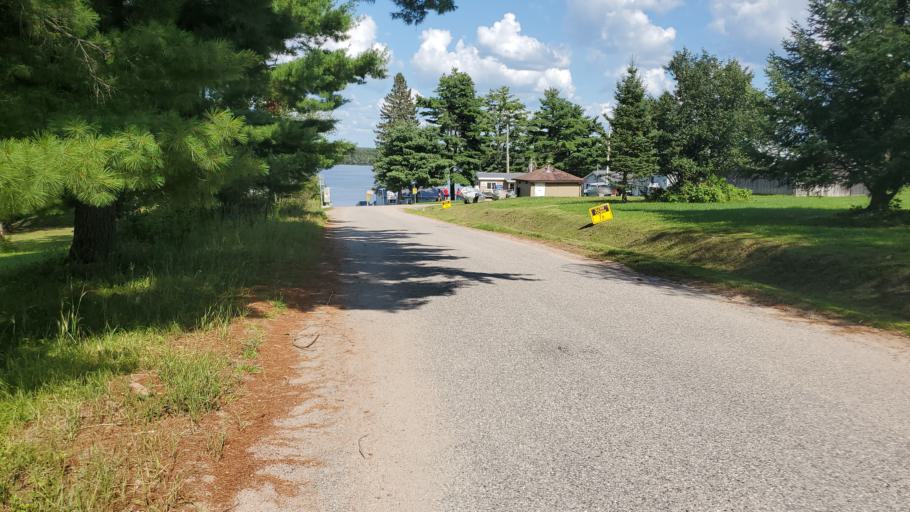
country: CA
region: Ontario
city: Powassan
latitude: 46.2187
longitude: -79.2302
